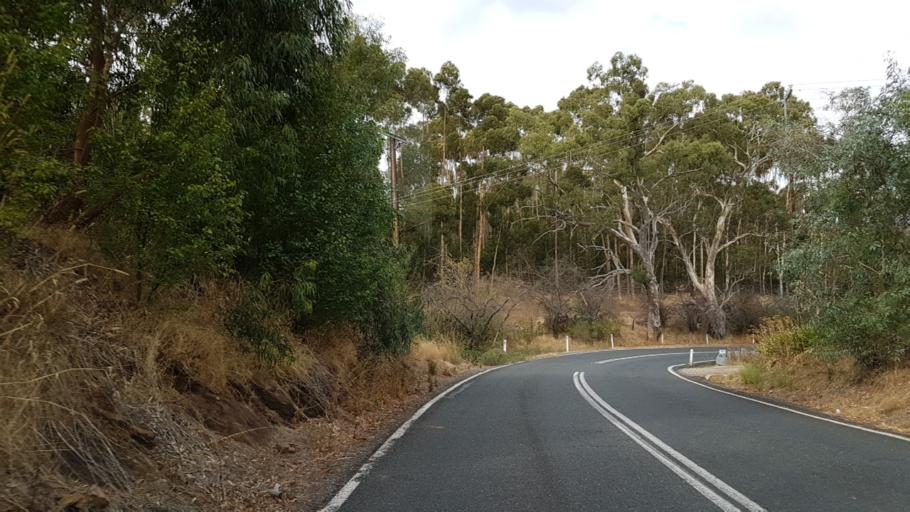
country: AU
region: South Australia
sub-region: Adelaide Hills
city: Gumeracha
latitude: -34.8233
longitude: 138.8471
